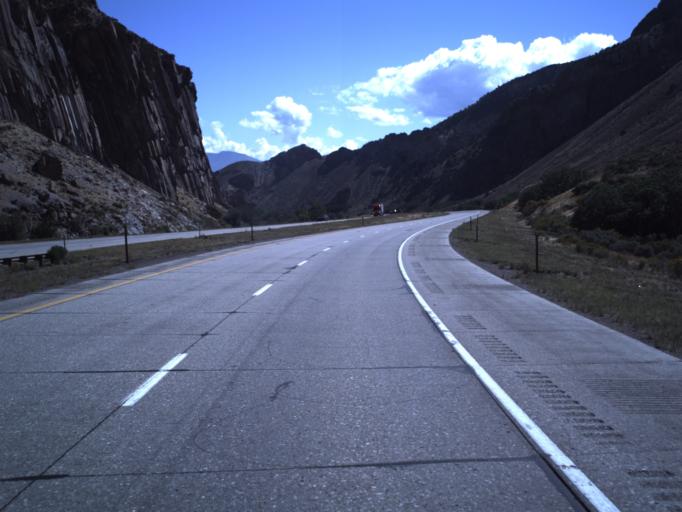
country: US
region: Utah
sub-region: Sevier County
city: Monroe
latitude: 38.5795
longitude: -112.2935
